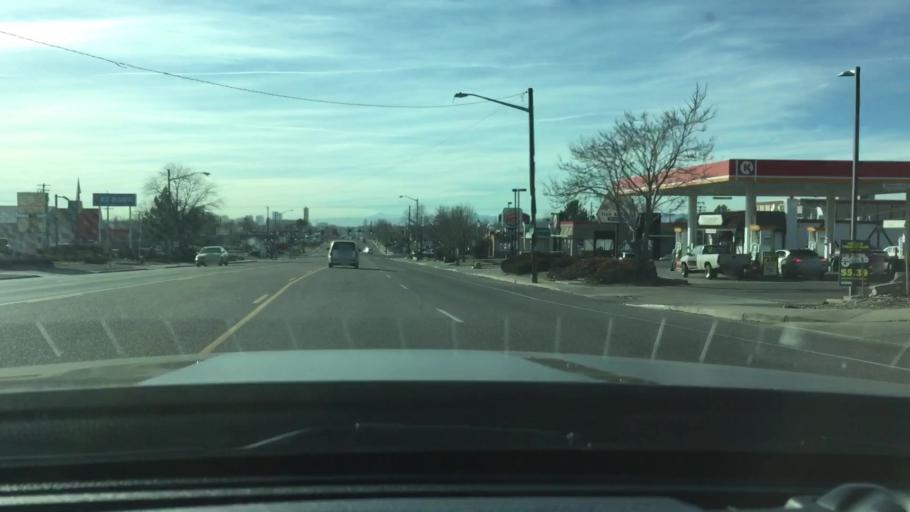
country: US
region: Colorado
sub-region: Adams County
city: Twin Lakes
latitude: 39.8294
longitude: -105.0064
